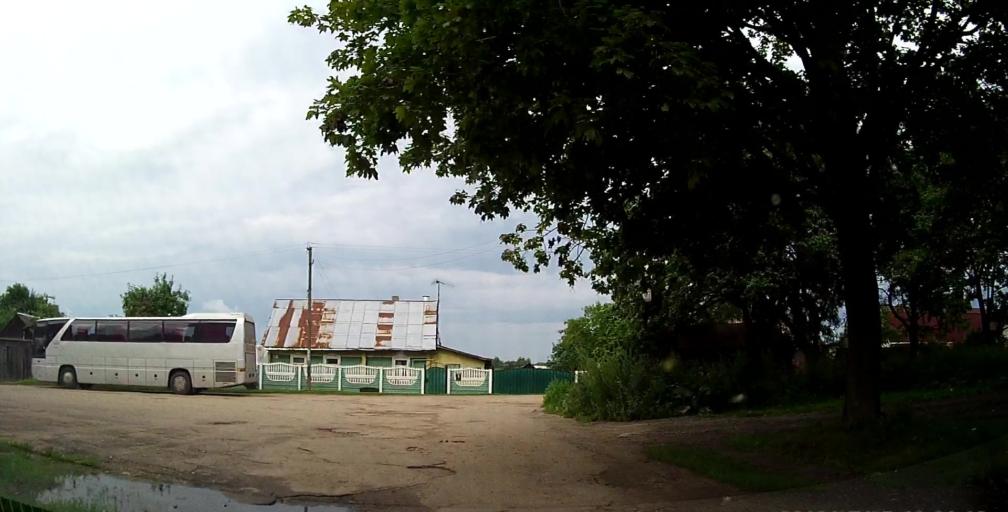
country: RU
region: Smolensk
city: Katyn'
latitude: 54.7716
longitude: 31.6829
